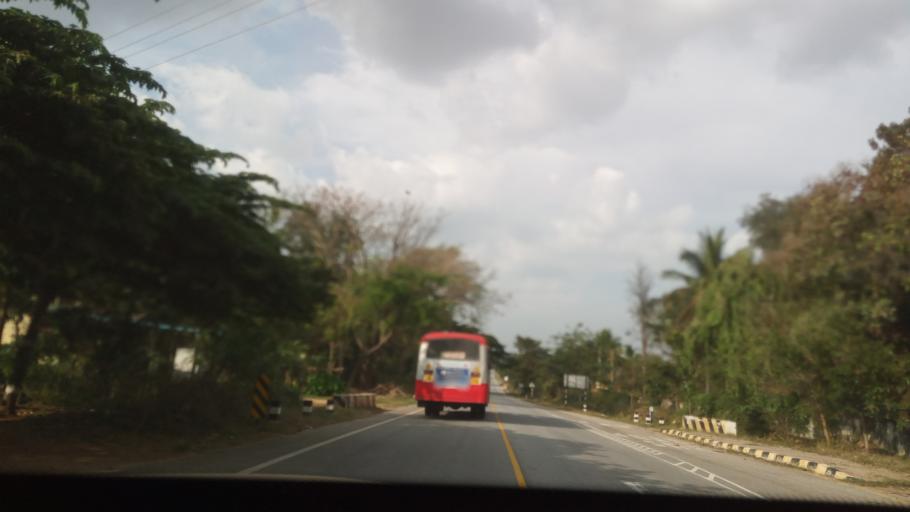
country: IN
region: Karnataka
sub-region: Tumkur
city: Kunigal
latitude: 12.8551
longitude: 77.0387
